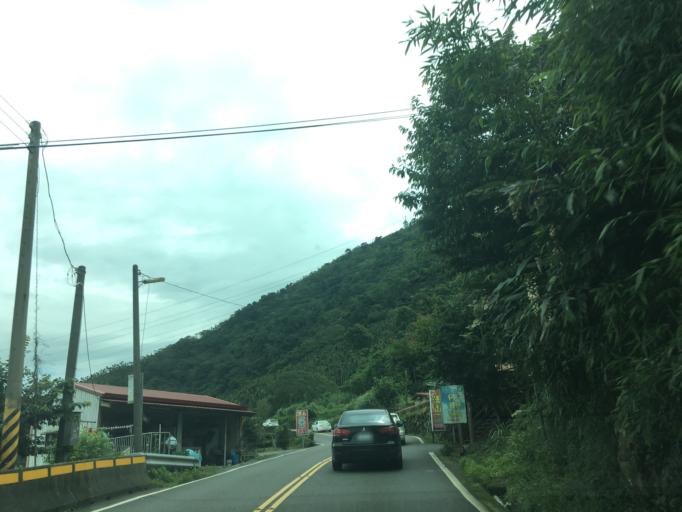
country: TW
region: Taiwan
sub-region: Yunlin
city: Douliu
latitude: 23.5623
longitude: 120.5921
